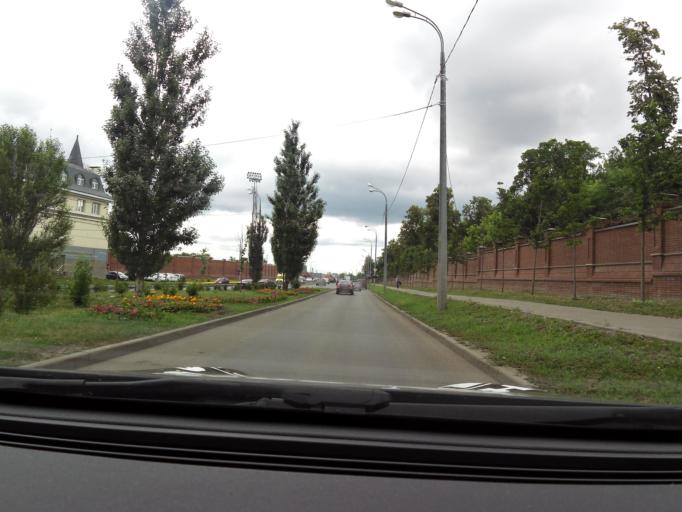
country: RU
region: Tatarstan
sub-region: Gorod Kazan'
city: Kazan
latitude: 55.7939
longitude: 49.1555
